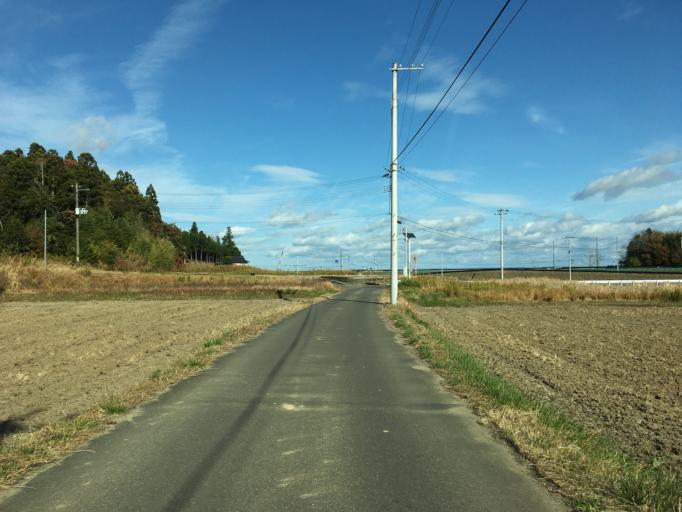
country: JP
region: Miyagi
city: Watari
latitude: 37.8964
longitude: 140.9221
